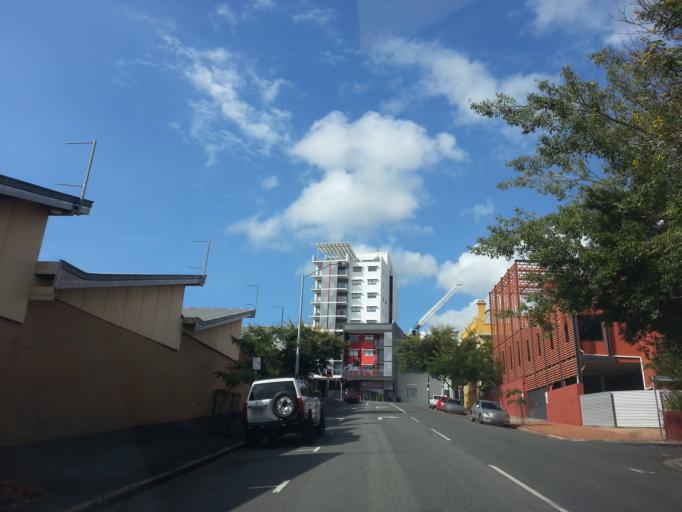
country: AU
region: Queensland
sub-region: Brisbane
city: Fortitude Valley
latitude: -27.4502
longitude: 153.0344
